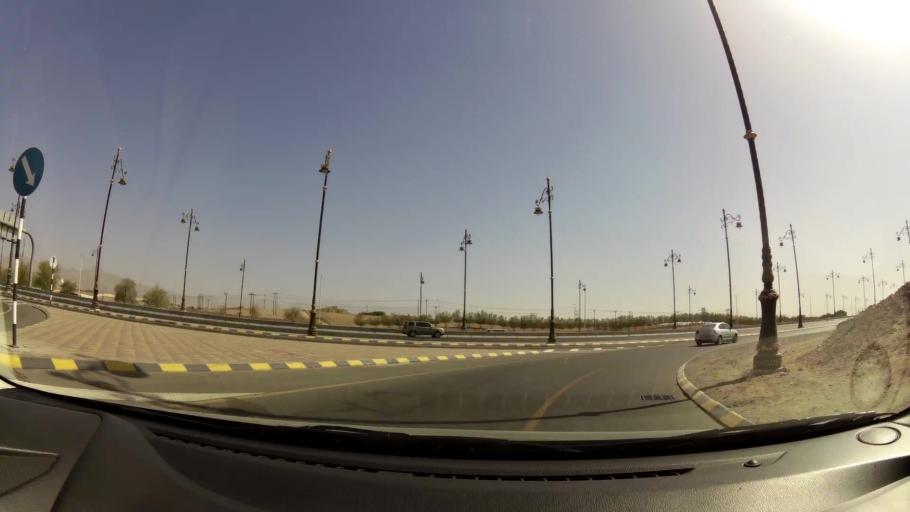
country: OM
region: Muhafazat Masqat
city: Bawshar
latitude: 23.5922
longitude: 58.3484
